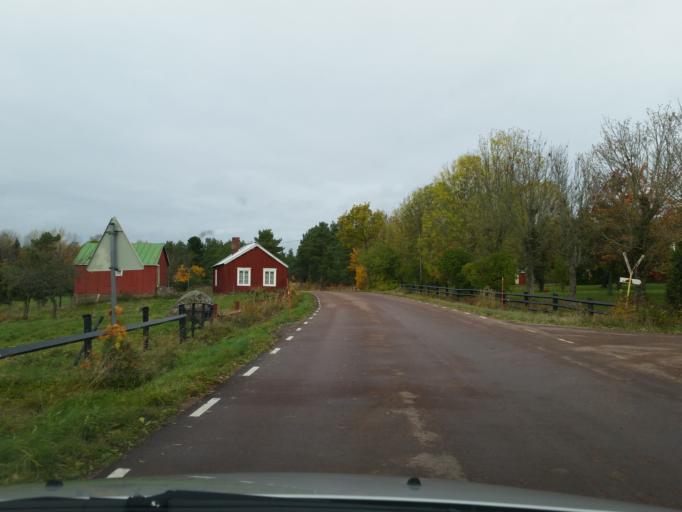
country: AX
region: Alands landsbygd
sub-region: Lemland
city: Lemland
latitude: 60.0173
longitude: 20.1300
